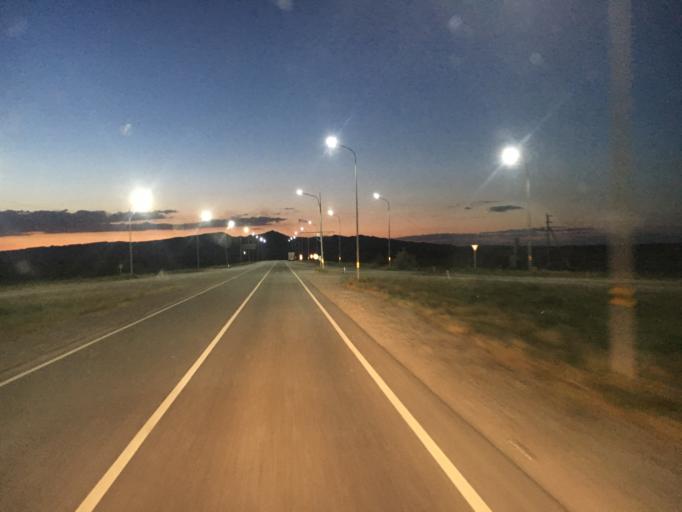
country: KZ
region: Zhambyl
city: Taraz
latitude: 42.8247
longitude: 71.1625
